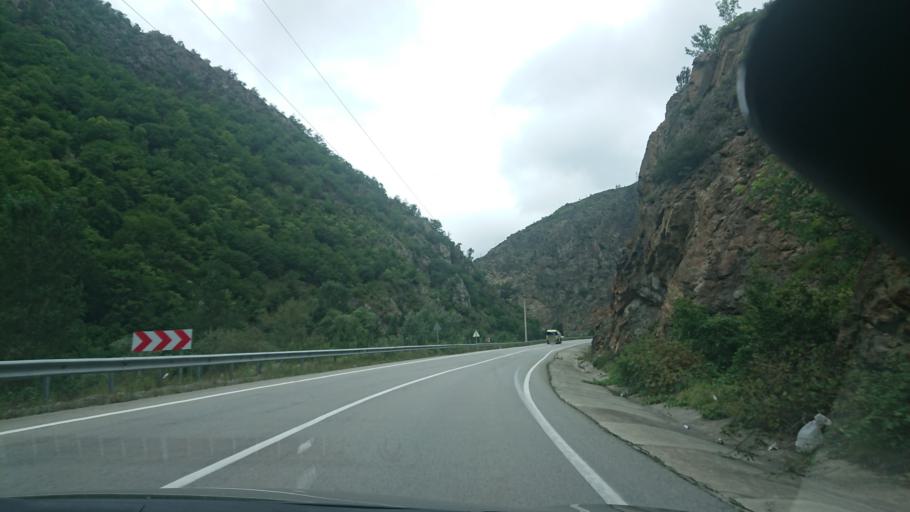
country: TR
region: Gumushane
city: Kurtun
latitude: 40.7322
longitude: 39.0105
